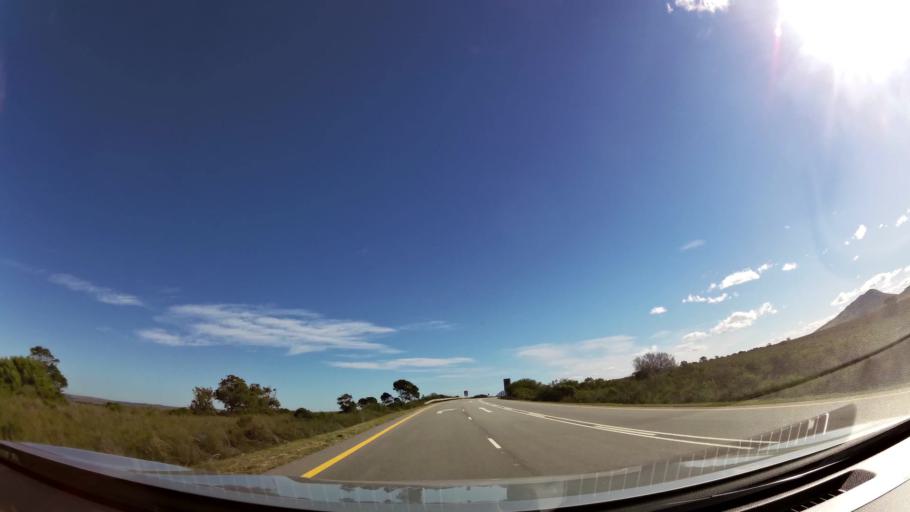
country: ZA
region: Eastern Cape
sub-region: Cacadu District Municipality
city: Kruisfontein
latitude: -34.0097
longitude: 24.6610
